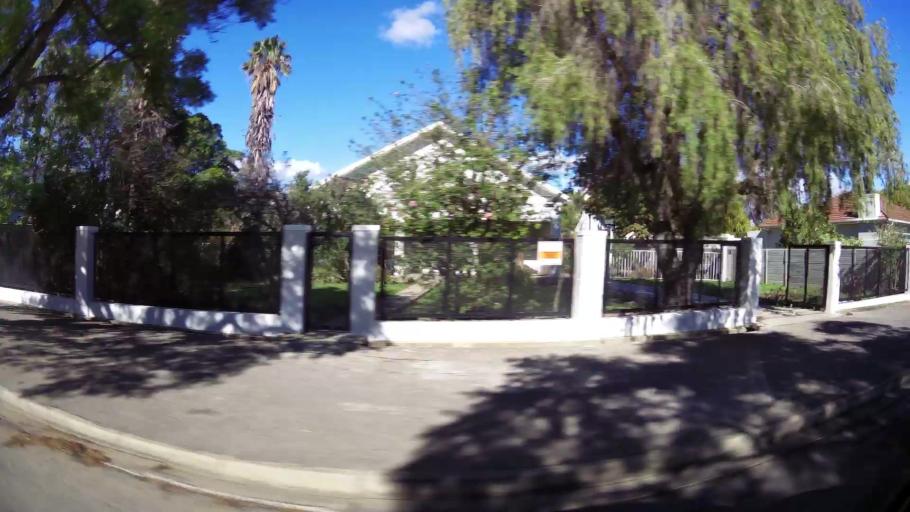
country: ZA
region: Western Cape
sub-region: Cape Winelands District Municipality
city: Ashton
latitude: -33.8006
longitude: 19.8855
